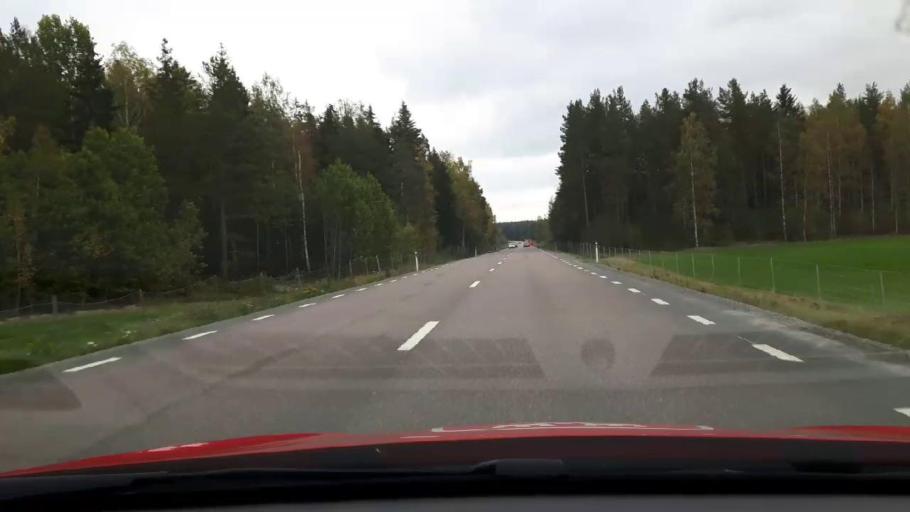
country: SE
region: Gaevleborg
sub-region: Bollnas Kommun
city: Bollnas
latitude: 61.3063
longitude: 16.4619
